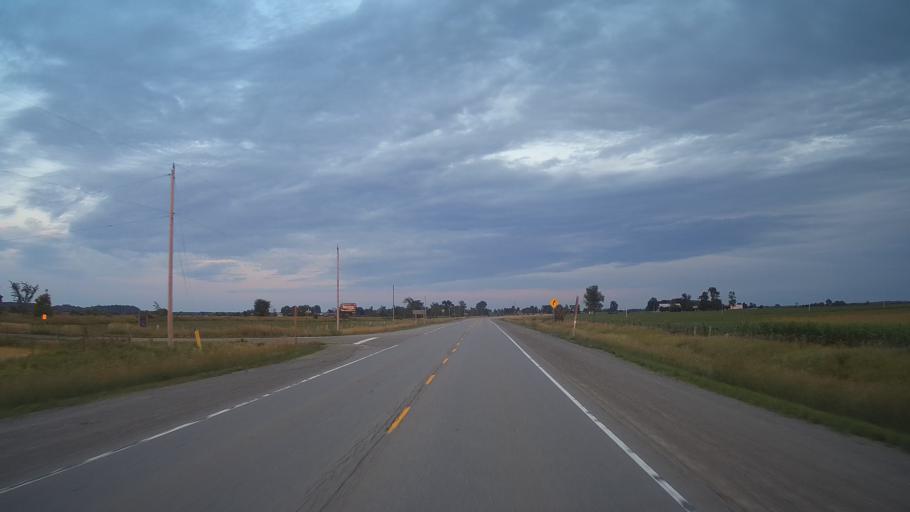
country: CA
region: Ontario
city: Pembroke
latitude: 45.6813
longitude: -76.9423
